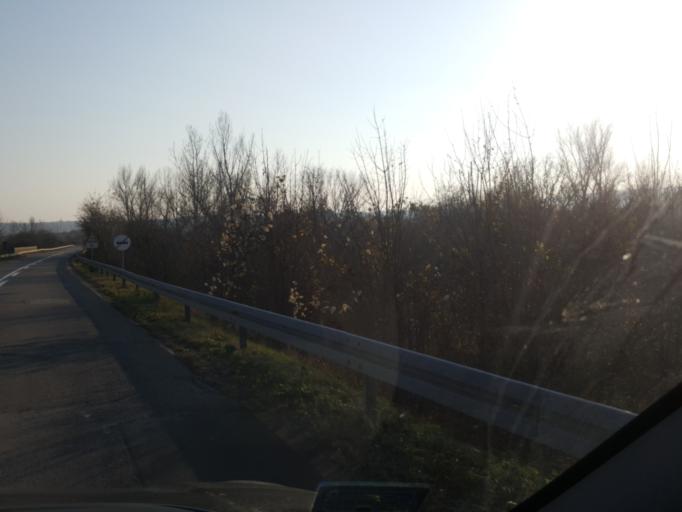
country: RS
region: Central Serbia
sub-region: Zajecarski Okrug
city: Zajecar
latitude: 44.1008
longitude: 22.3480
